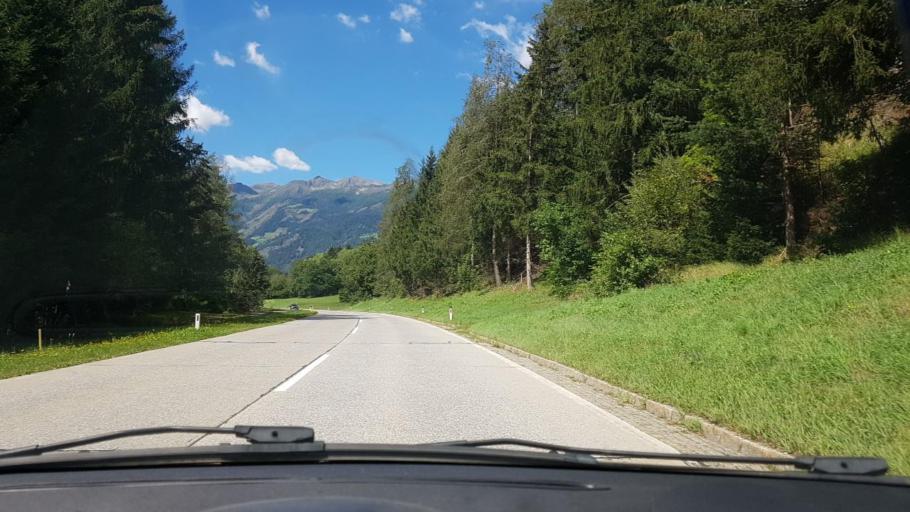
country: AT
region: Carinthia
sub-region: Politischer Bezirk Spittal an der Drau
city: Flattach
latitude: 46.9357
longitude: 13.1456
